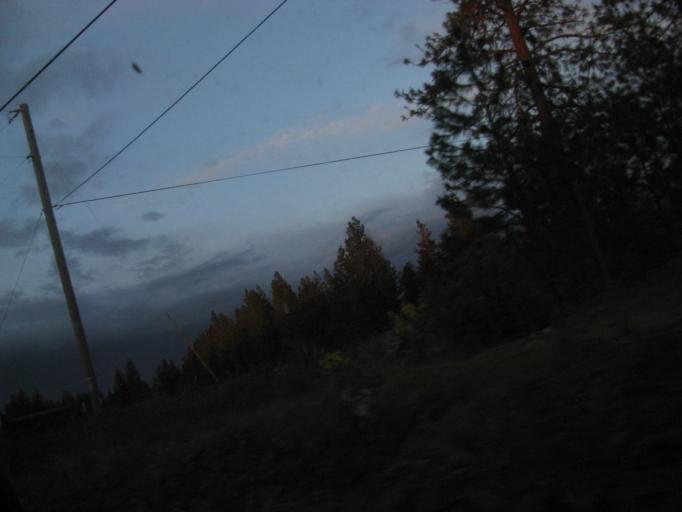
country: US
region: Washington
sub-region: Spokane County
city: Cheney
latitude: 47.4564
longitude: -117.6088
